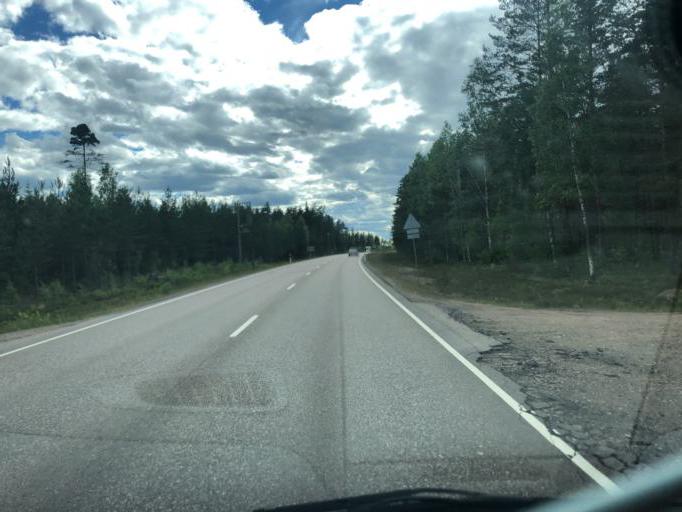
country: FI
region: Southern Savonia
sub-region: Mikkeli
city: Maentyharju
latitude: 61.0992
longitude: 27.0955
